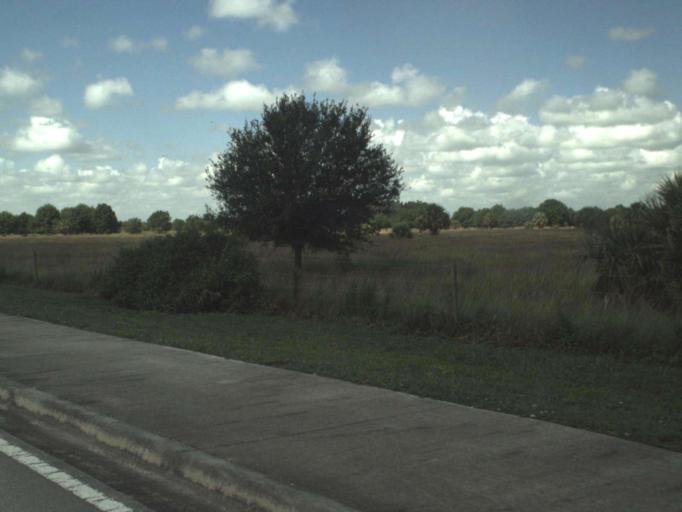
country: US
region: Florida
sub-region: Indian River County
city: Vero Beach South
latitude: 27.5930
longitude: -80.4474
